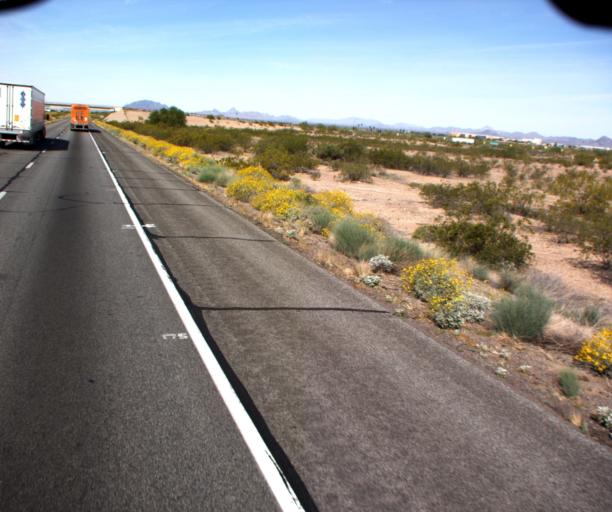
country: US
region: Arizona
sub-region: Maricopa County
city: Buckeye
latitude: 33.4813
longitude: -112.8643
